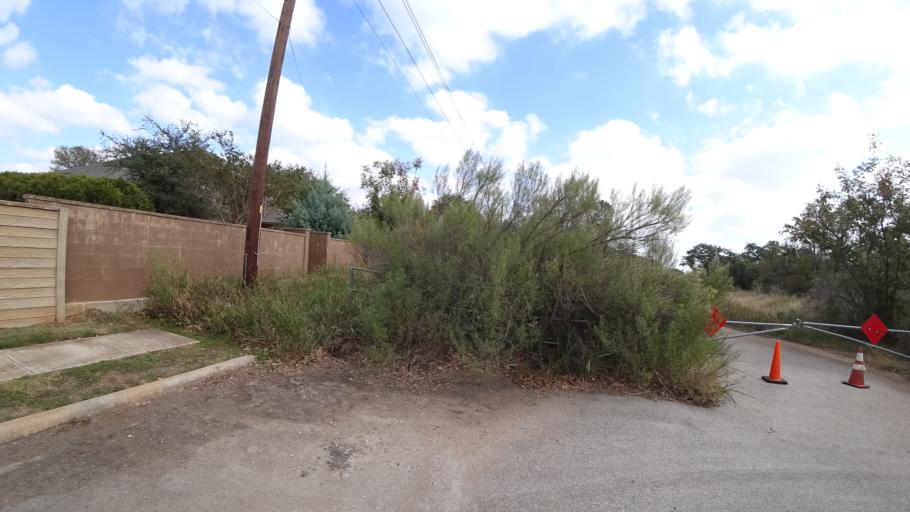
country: US
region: Texas
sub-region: Travis County
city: Shady Hollow
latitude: 30.1733
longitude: -97.8504
